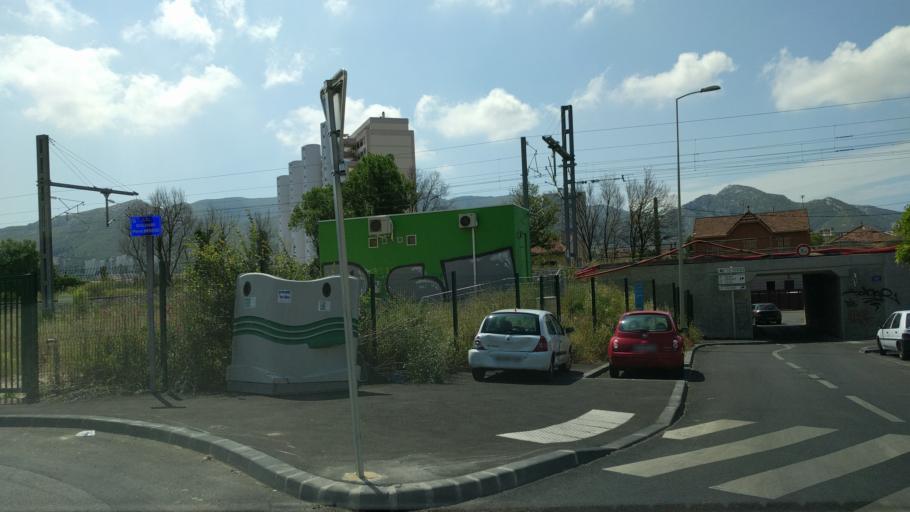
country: FR
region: Provence-Alpes-Cote d'Azur
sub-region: Departement des Bouches-du-Rhone
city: Marseille 11
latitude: 43.2899
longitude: 5.4364
